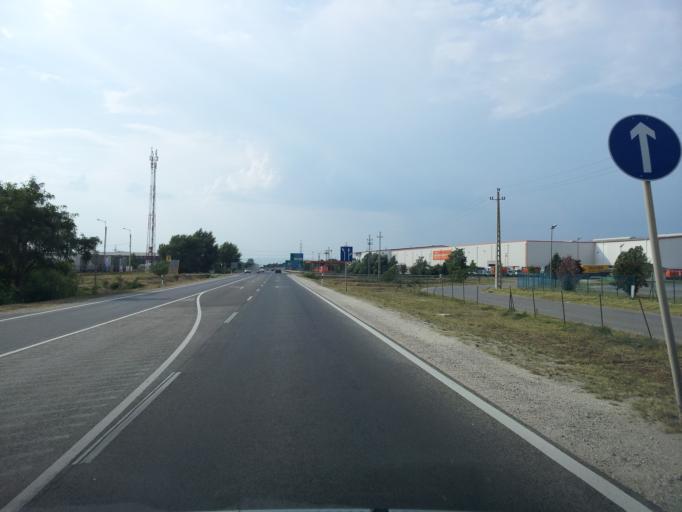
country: HU
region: Pest
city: Dunaharaszti
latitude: 47.3621
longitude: 19.1202
